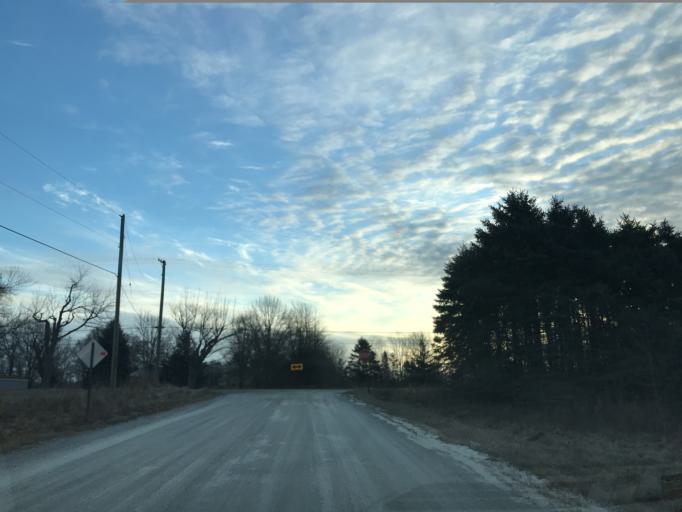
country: US
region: Michigan
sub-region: Macomb County
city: Armada
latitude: 42.9013
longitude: -82.8839
